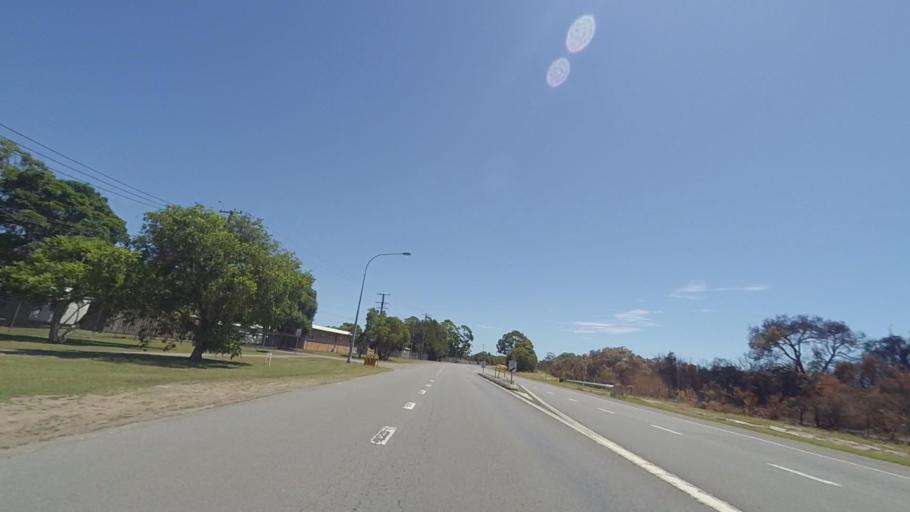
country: AU
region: New South Wales
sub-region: Port Stephens Shire
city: Medowie
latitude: -32.7933
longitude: 151.8532
